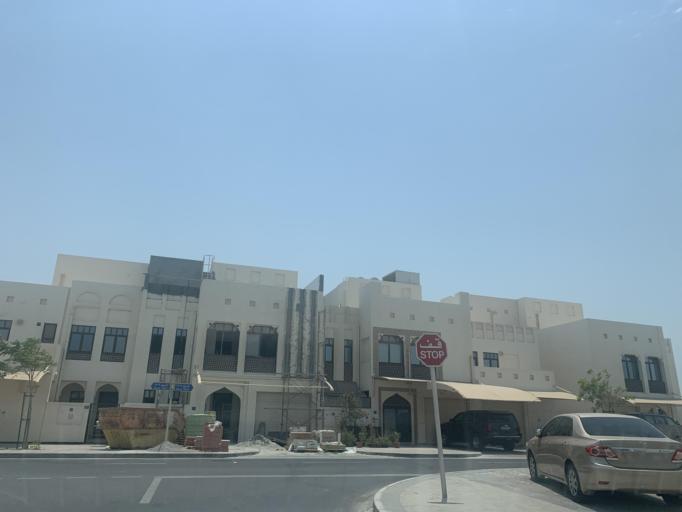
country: BH
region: Muharraq
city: Al Hadd
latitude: 26.2389
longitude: 50.6735
